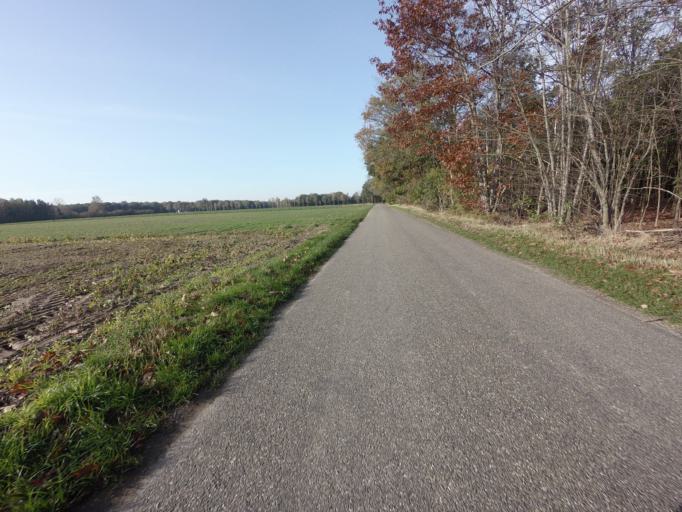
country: NL
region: Limburg
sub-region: Gemeente Echt-Susteren
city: Koningsbosch
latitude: 51.0599
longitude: 5.9280
